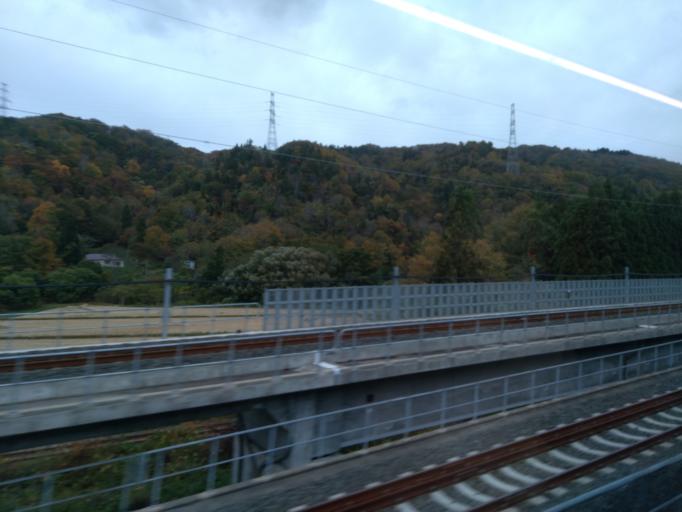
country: JP
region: Aomori
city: Goshogawara
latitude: 41.1483
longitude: 140.5128
